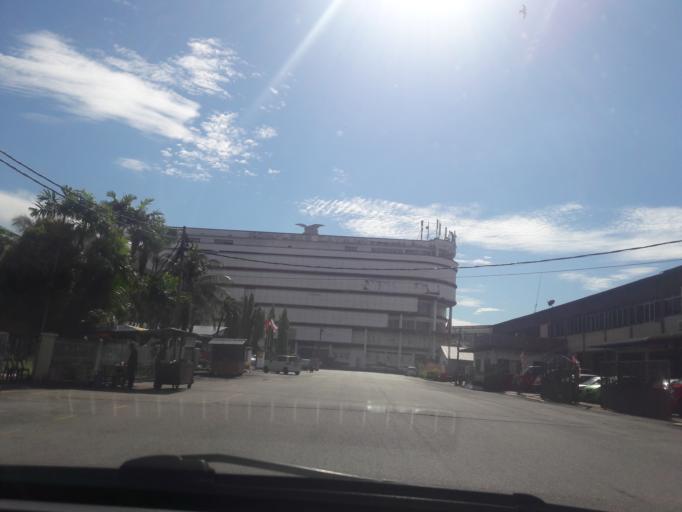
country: MY
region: Kedah
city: Sungai Petani
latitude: 5.6399
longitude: 100.4859
